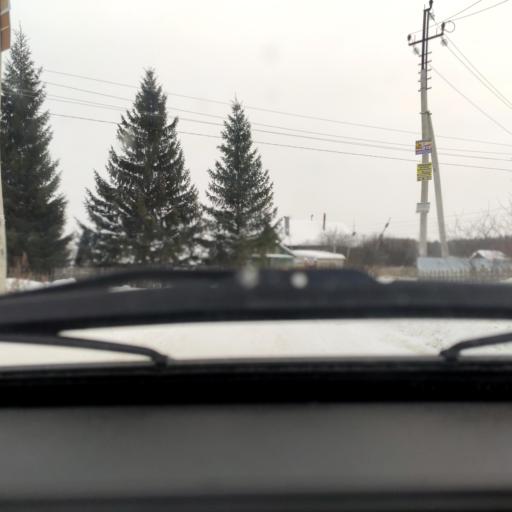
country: RU
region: Bashkortostan
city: Mikhaylovka
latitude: 54.8534
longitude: 55.8792
